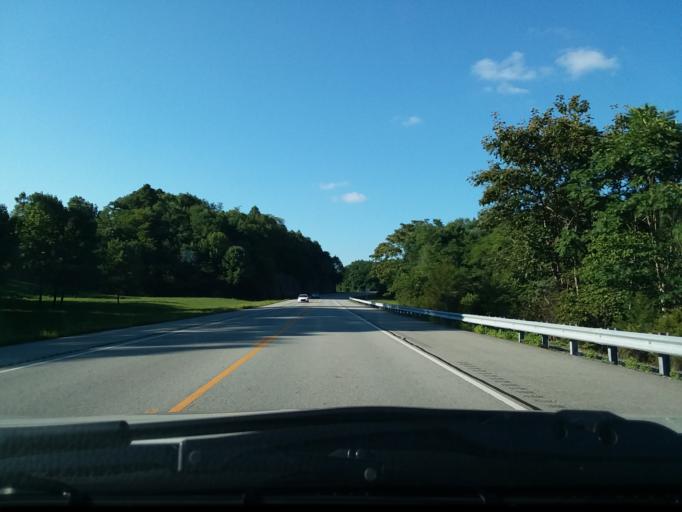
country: US
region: Tennessee
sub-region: Clay County
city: Celina
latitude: 36.5739
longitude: -85.4477
